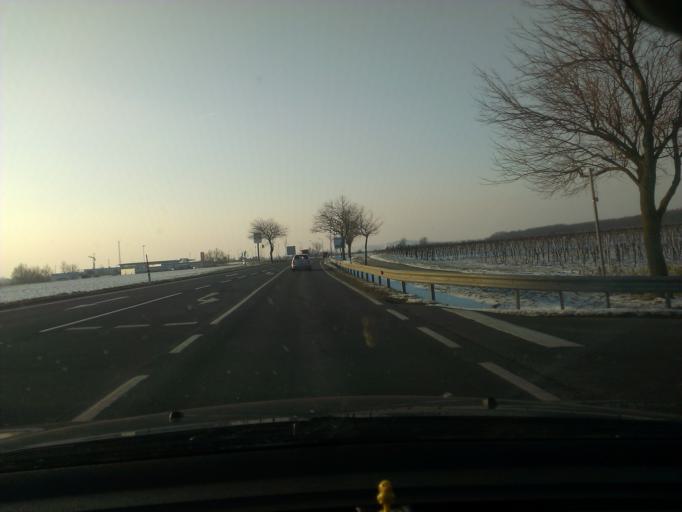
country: AT
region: Burgenland
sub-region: Eisenstadt-Umgebung
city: Donnerskirchen
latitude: 47.8809
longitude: 16.6478
